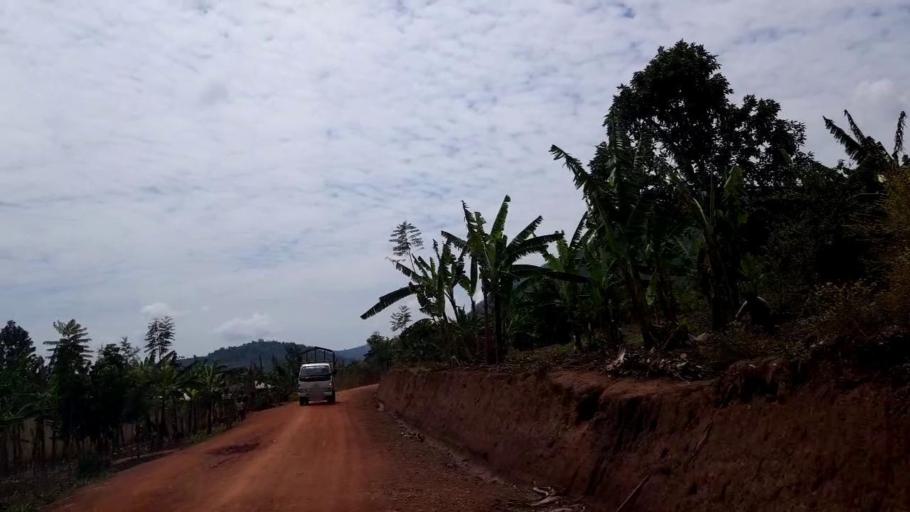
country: RW
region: Northern Province
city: Byumba
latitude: -1.5060
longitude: 30.1943
